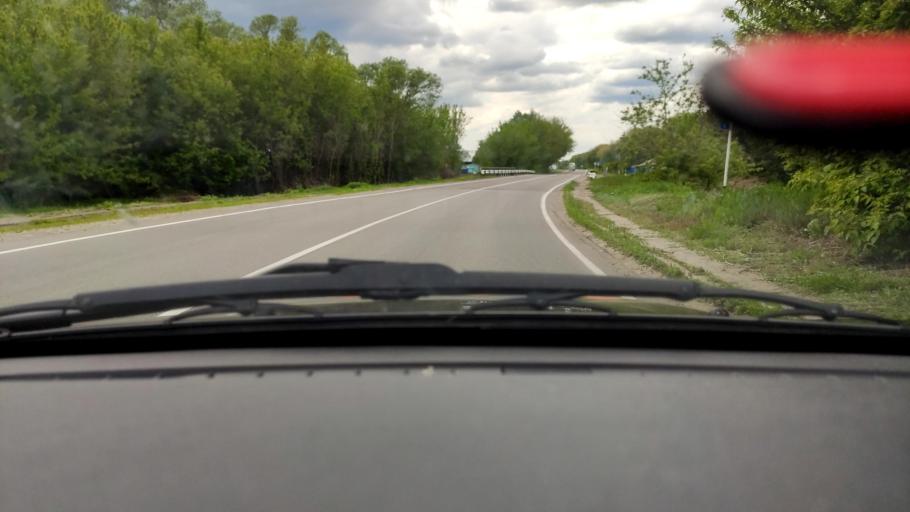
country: RU
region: Voronezj
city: Ostrogozhsk
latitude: 51.0547
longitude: 38.9157
